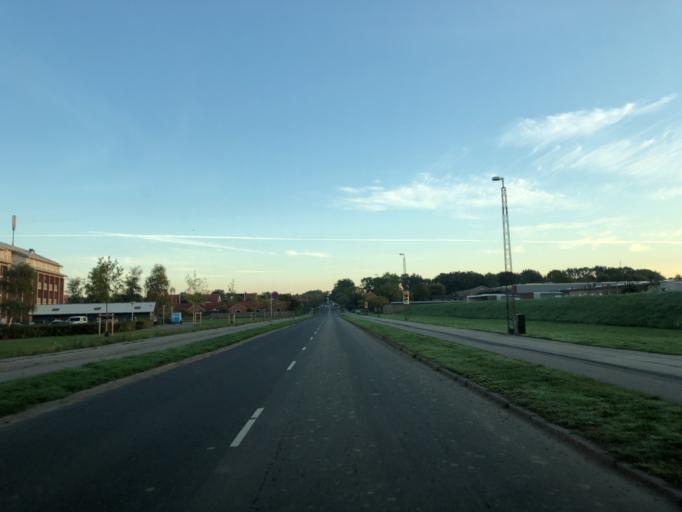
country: DK
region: South Denmark
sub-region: Sonderborg Kommune
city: Sonderborg
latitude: 54.9002
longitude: 9.8092
